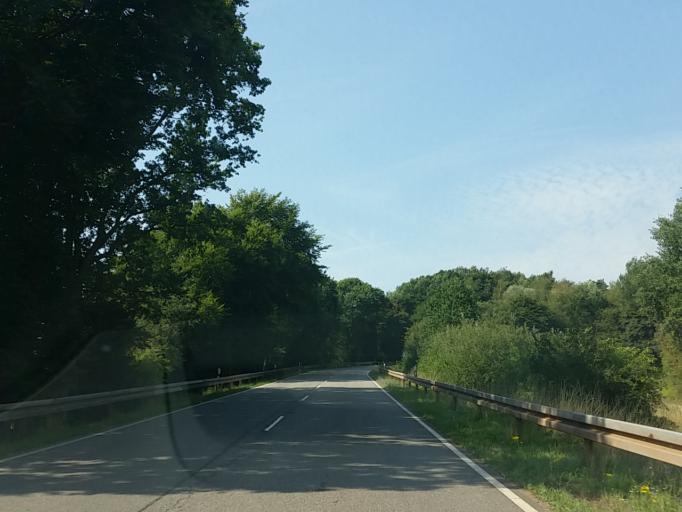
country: DE
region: Saarland
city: Schmelz
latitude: 49.4065
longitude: 6.8714
